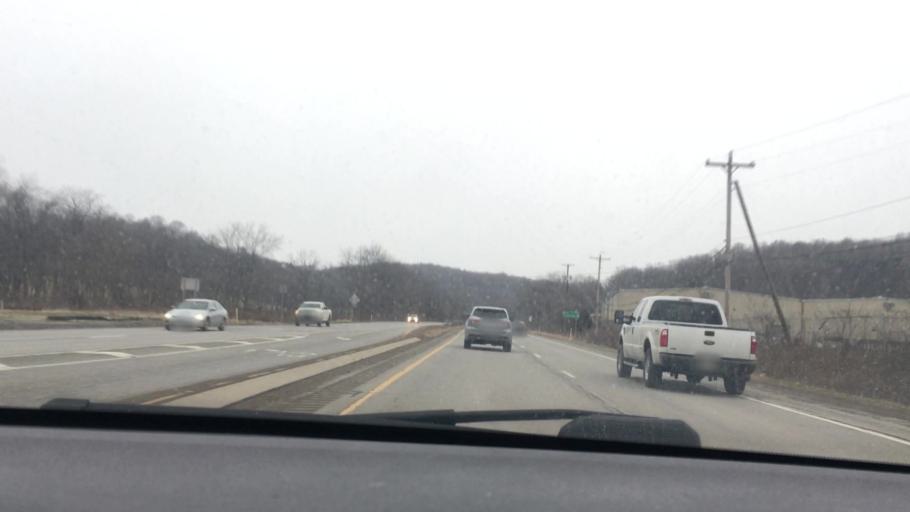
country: US
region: Pennsylvania
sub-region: Beaver County
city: Big Beaver
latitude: 40.8051
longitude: -80.4467
